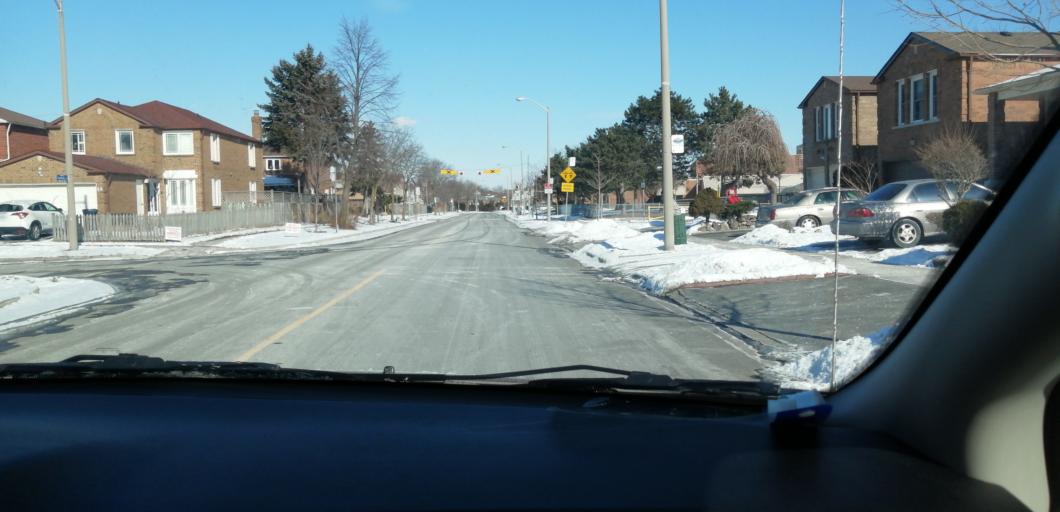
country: CA
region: Ontario
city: Scarborough
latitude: 43.8137
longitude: -79.2197
